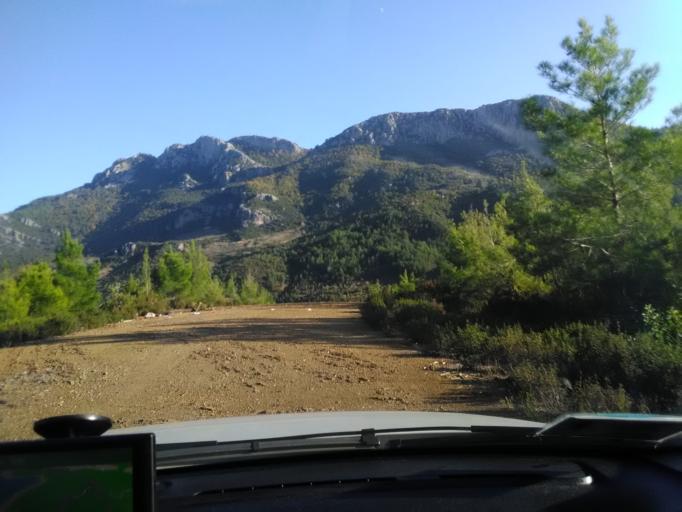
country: TR
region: Antalya
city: Gazipasa
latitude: 36.3088
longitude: 32.3949
